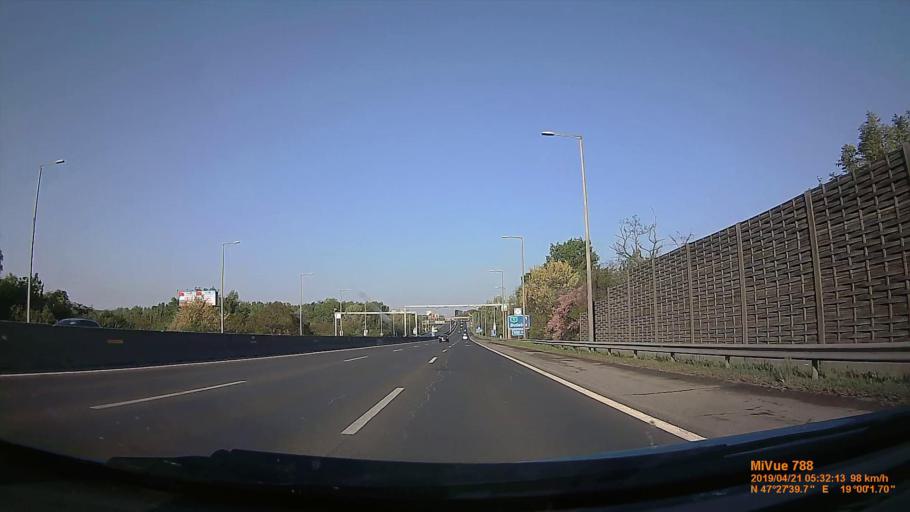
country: HU
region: Budapest
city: Budapest XII. keruelet
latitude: 47.4602
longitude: 19.0007
